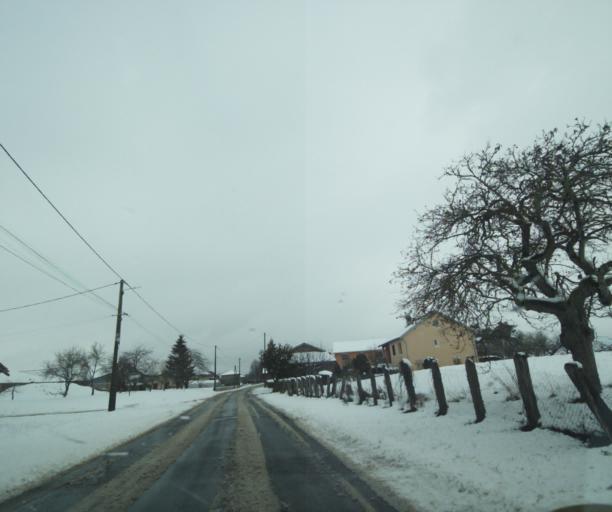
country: FR
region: Champagne-Ardenne
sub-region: Departement de la Haute-Marne
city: Montier-en-Der
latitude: 48.4649
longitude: 4.7521
